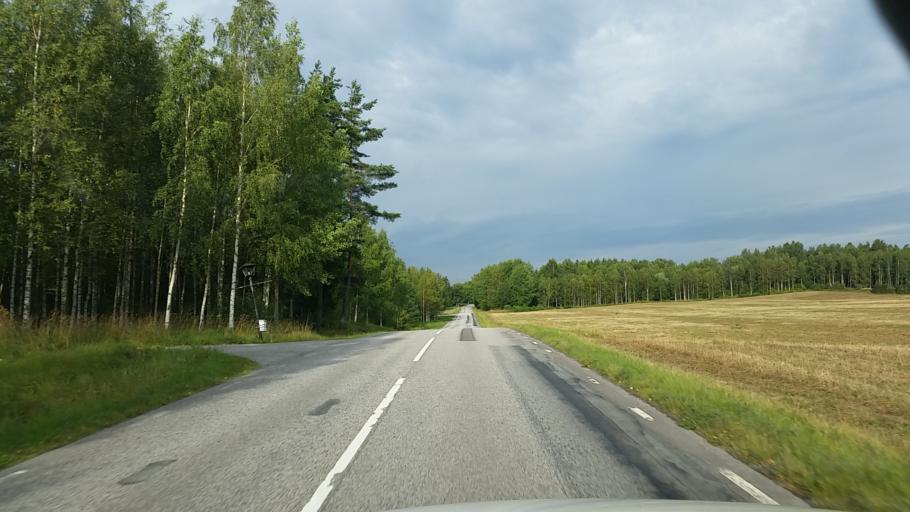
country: SE
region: OErebro
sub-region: Lindesbergs Kommun
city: Fellingsbro
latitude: 59.3258
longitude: 15.4898
